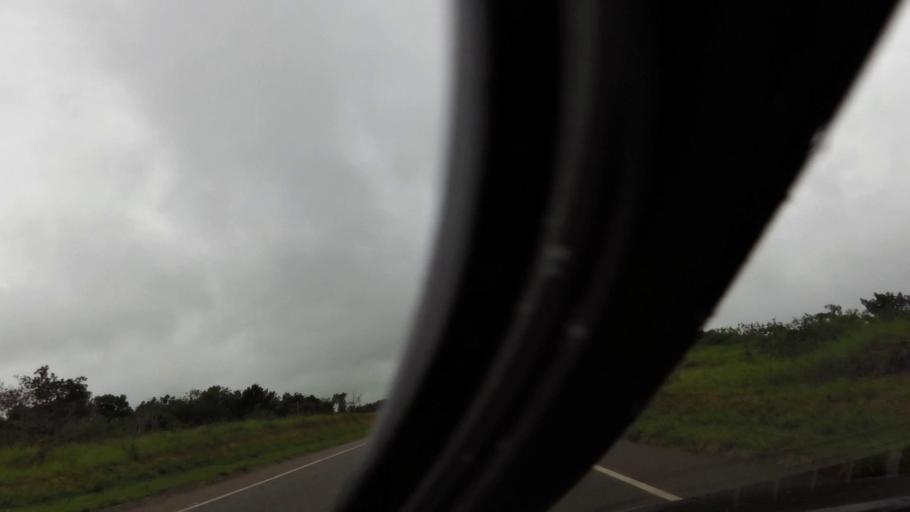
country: BR
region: Espirito Santo
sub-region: Guarapari
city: Guarapari
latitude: -20.7155
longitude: -40.5765
